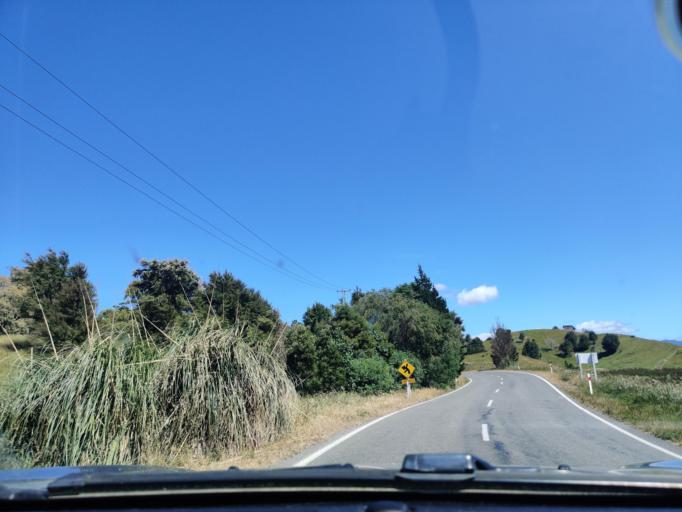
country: NZ
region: Wellington
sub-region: South Wairarapa District
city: Waipawa
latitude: -41.2278
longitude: 175.3396
